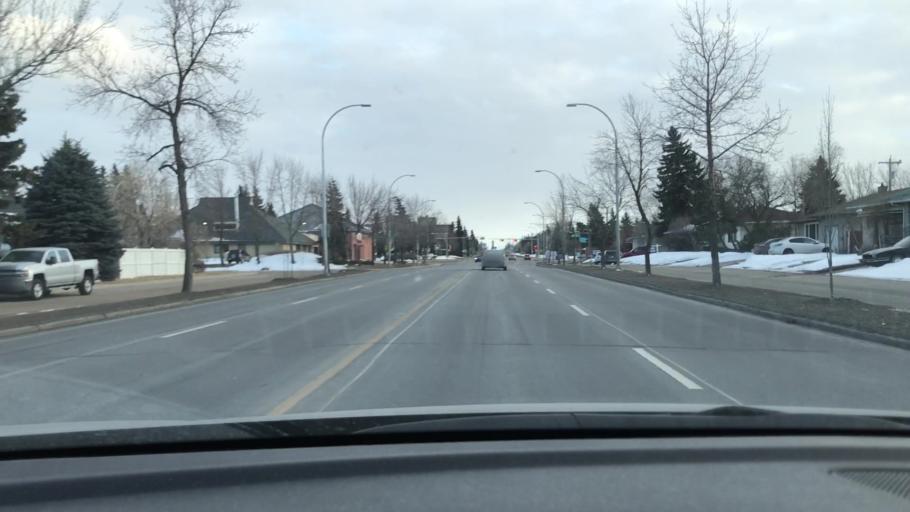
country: CA
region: Alberta
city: Edmonton
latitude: 53.5275
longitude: -113.4428
